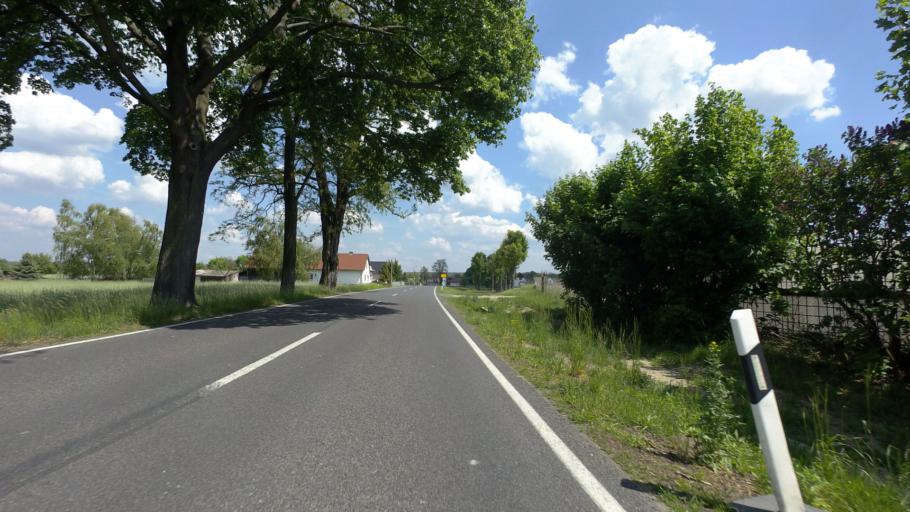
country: DE
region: Brandenburg
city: Straupitz
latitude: 51.9273
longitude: 14.1622
